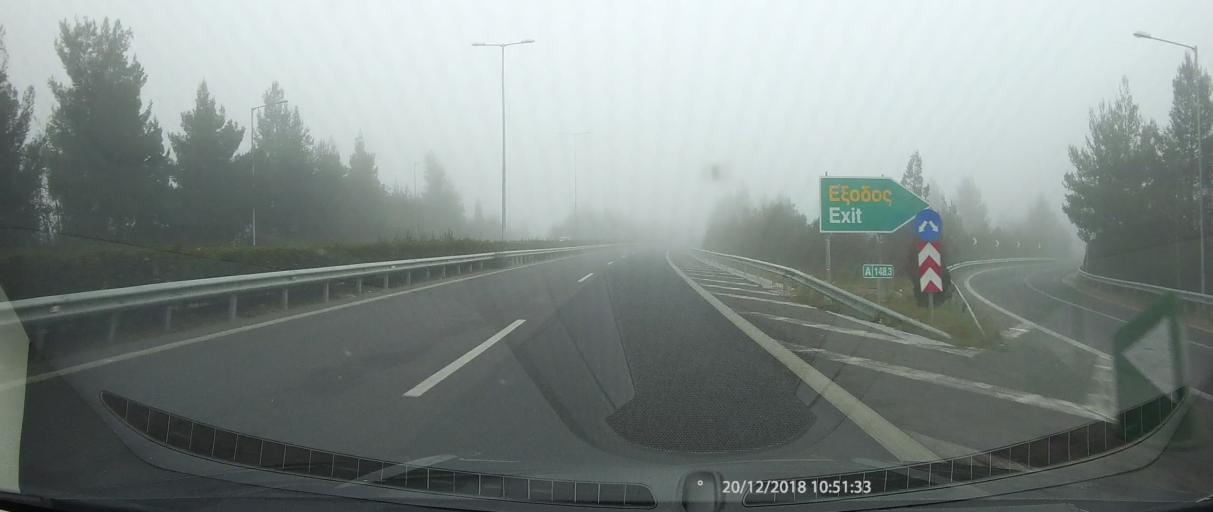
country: GR
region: Peloponnese
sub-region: Nomos Arkadias
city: Tripoli
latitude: 37.5888
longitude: 22.4356
